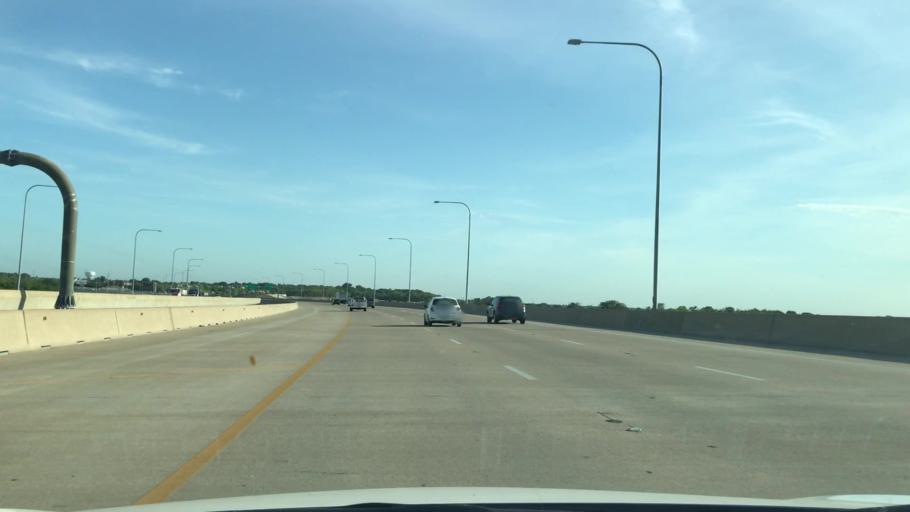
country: US
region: Texas
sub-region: Dallas County
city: Rowlett
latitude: 32.8713
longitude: -96.5529
